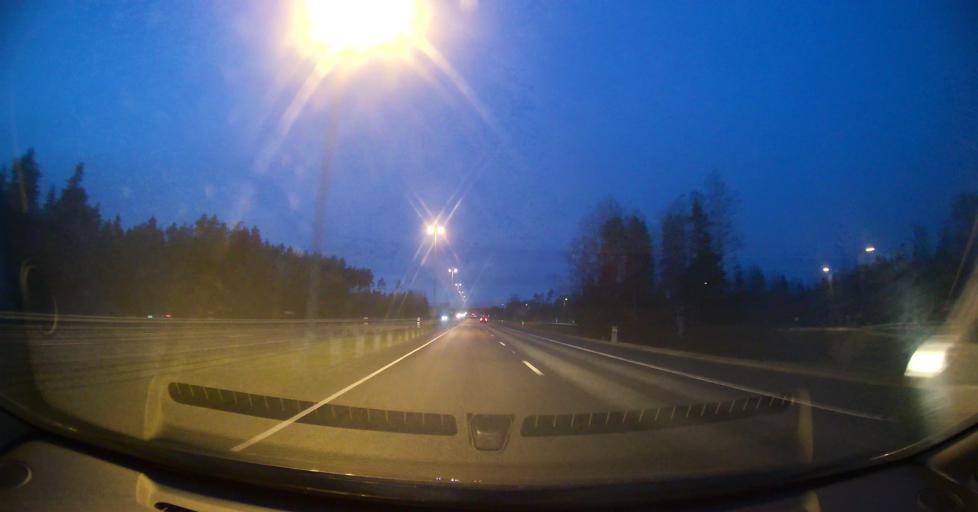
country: EE
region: Harju
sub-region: Rae vald
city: Vaida
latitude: 59.2229
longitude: 25.0387
